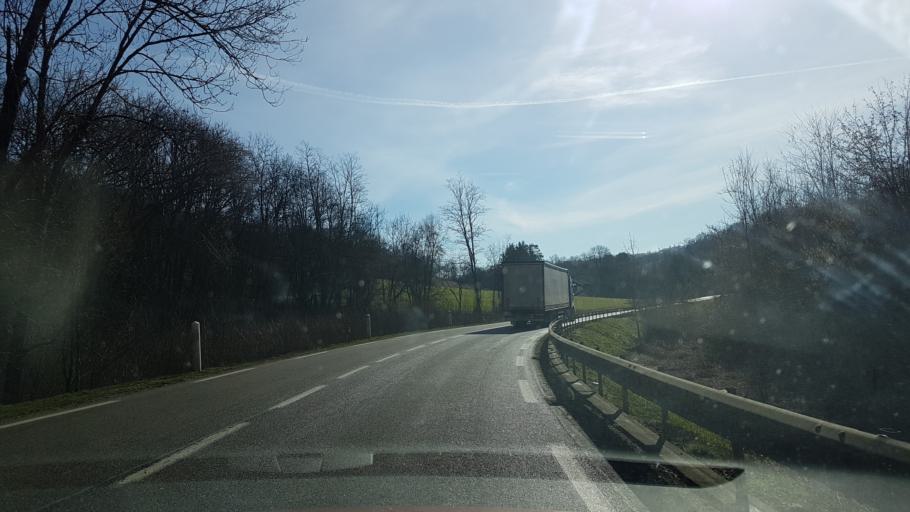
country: FR
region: Rhone-Alpes
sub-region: Departement de la Haute-Savoie
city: Frangy
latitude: 46.0260
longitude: 5.9006
